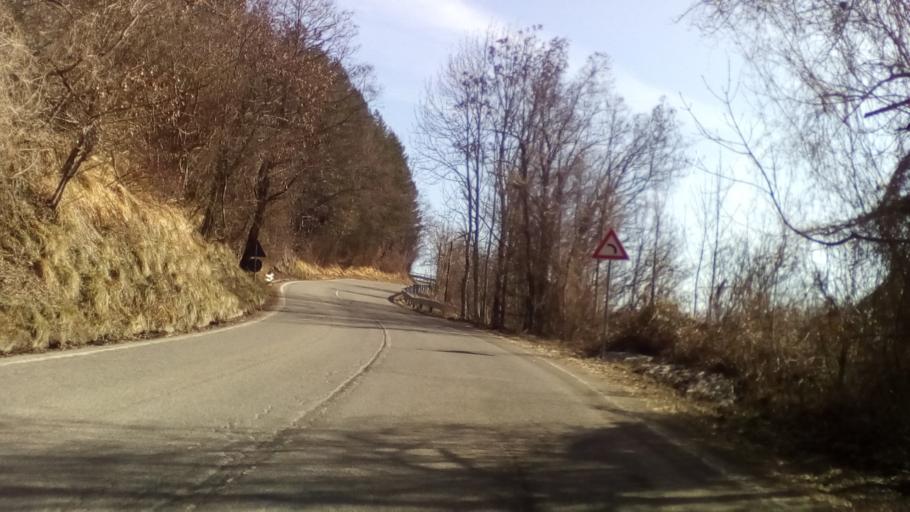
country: IT
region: Emilia-Romagna
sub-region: Provincia di Modena
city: Riolunato
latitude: 44.2568
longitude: 10.6475
